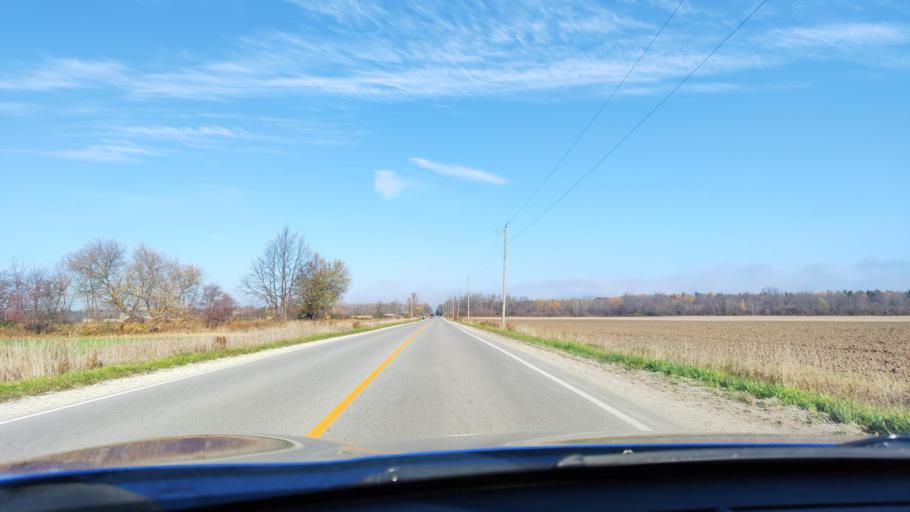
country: CA
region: Ontario
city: Wasaga Beach
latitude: 44.3975
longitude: -80.0572
